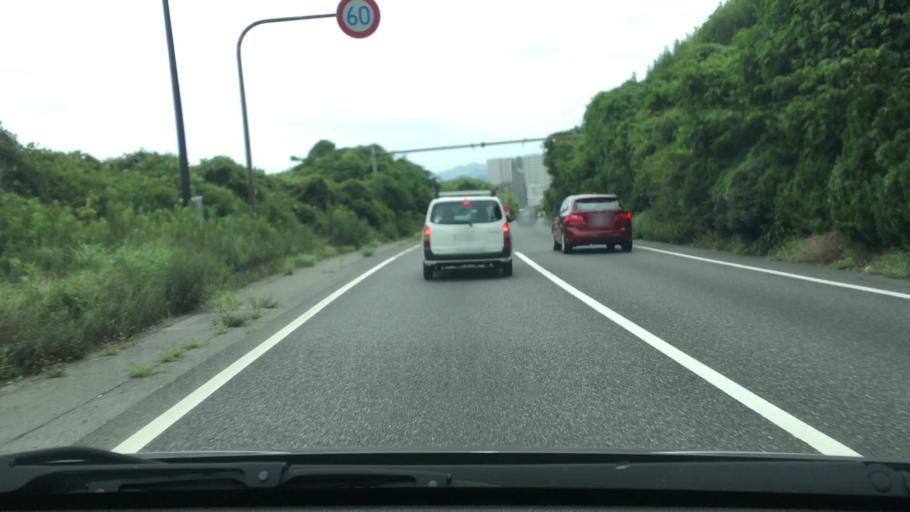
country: JP
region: Hiroshima
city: Hatsukaichi
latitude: 34.3793
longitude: 132.3892
